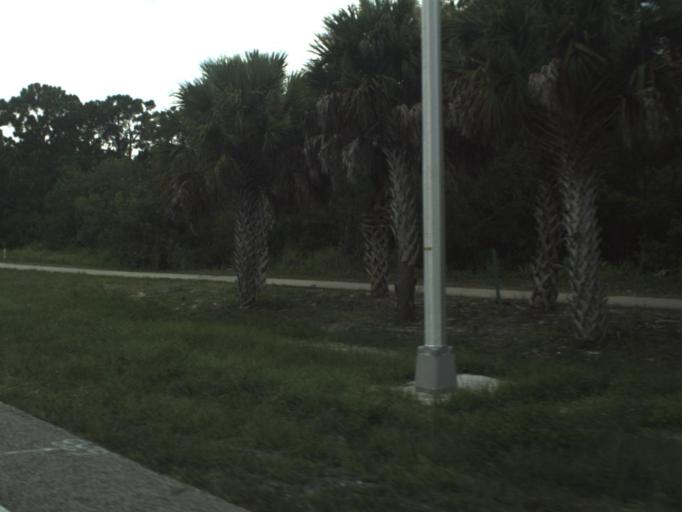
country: US
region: Florida
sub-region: Martin County
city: Hobe Sound
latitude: 27.1029
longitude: -80.1635
